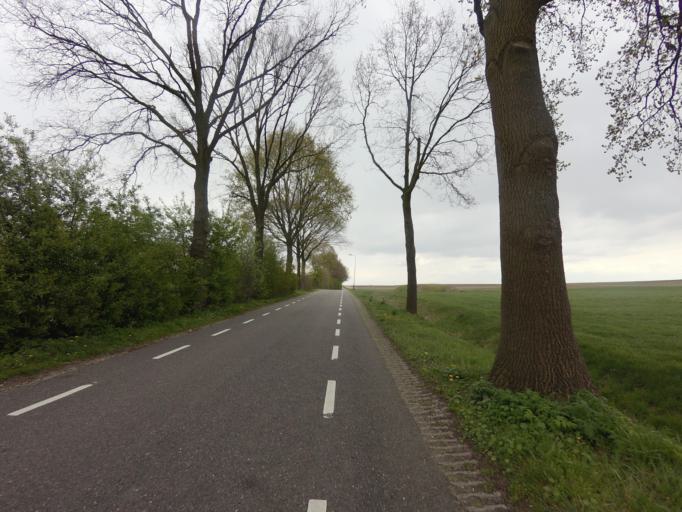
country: NL
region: Utrecht
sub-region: Gemeente Utrechtse Heuvelrug
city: Overberg
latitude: 52.0501
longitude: 5.5228
